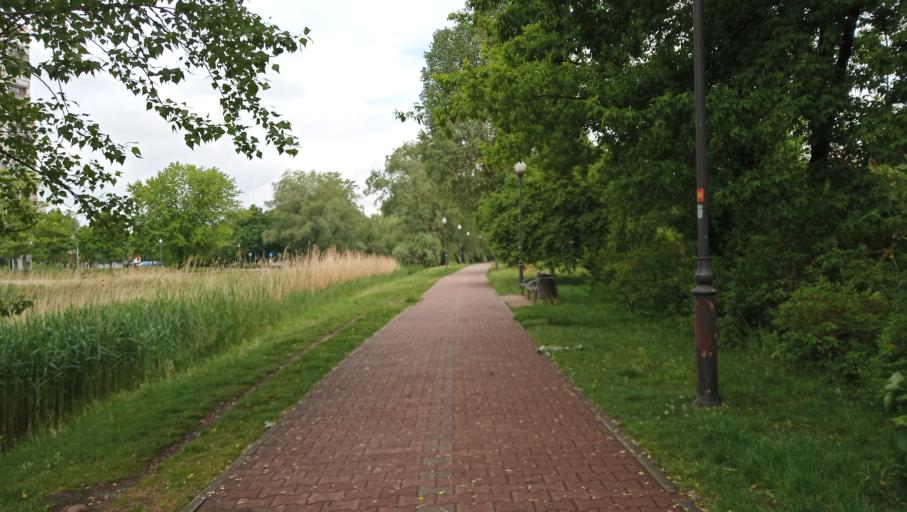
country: PL
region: Masovian Voivodeship
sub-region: Warszawa
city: Zoliborz
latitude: 52.2842
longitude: 20.9807
